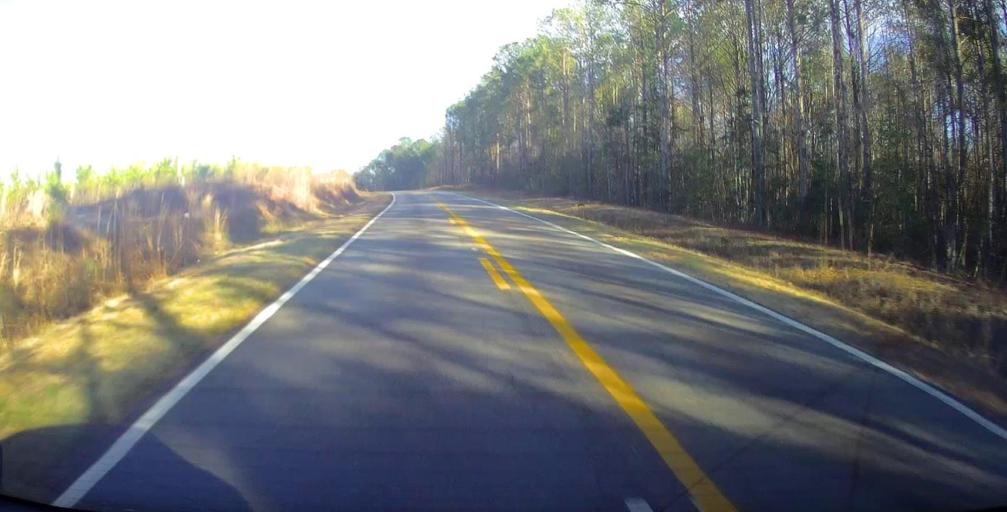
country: US
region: Georgia
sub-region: Crawford County
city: Roberta
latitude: 32.7711
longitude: -84.1063
